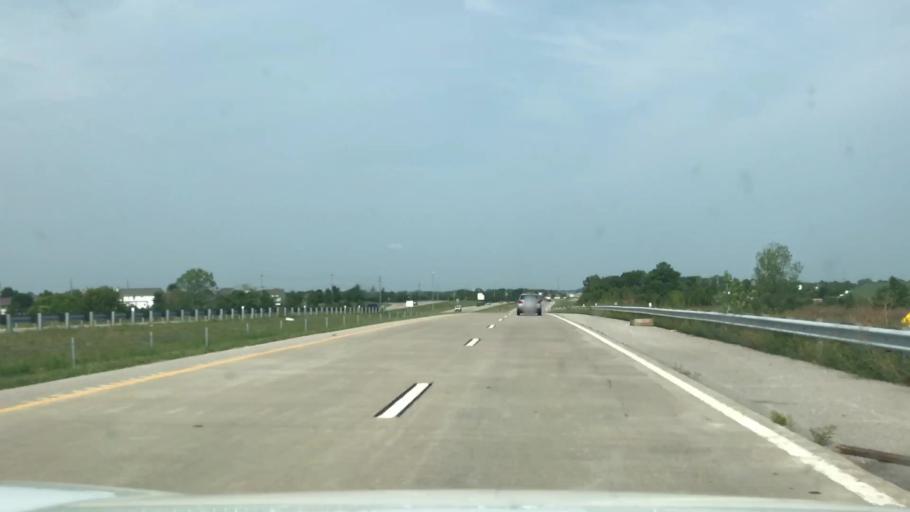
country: US
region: Missouri
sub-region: Saint Charles County
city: Dardenne Prairie
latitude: 38.7544
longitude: -90.7026
